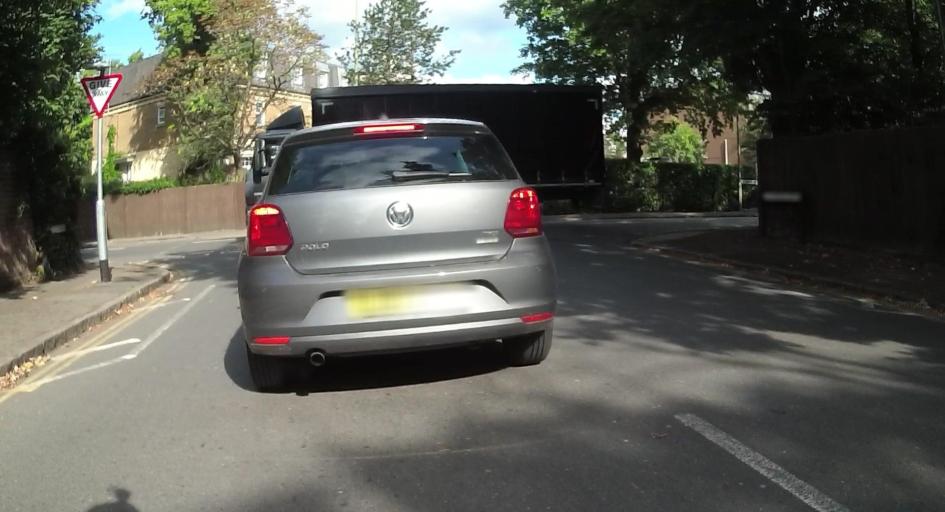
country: GB
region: England
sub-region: Surrey
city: Weybridge
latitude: 51.3661
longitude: -0.4423
